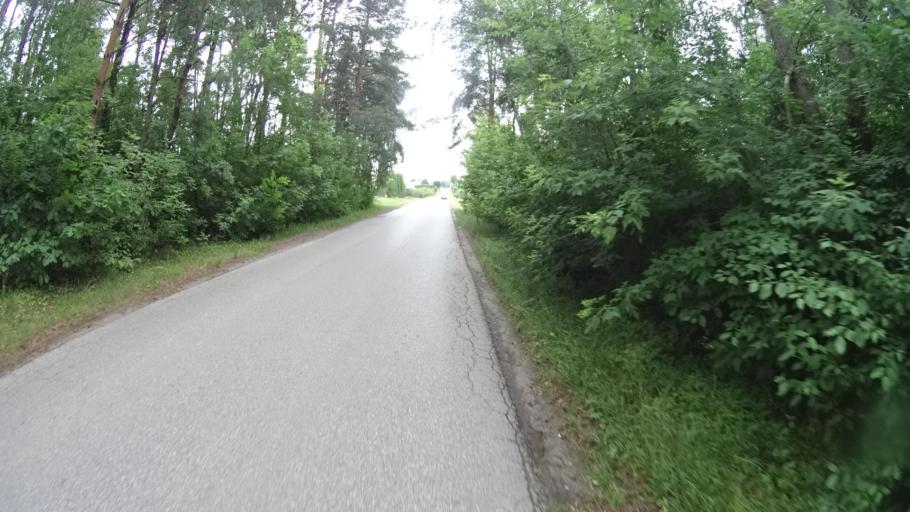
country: PL
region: Masovian Voivodeship
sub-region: Powiat grojecki
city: Belsk Duzy
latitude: 51.7977
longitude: 20.8588
